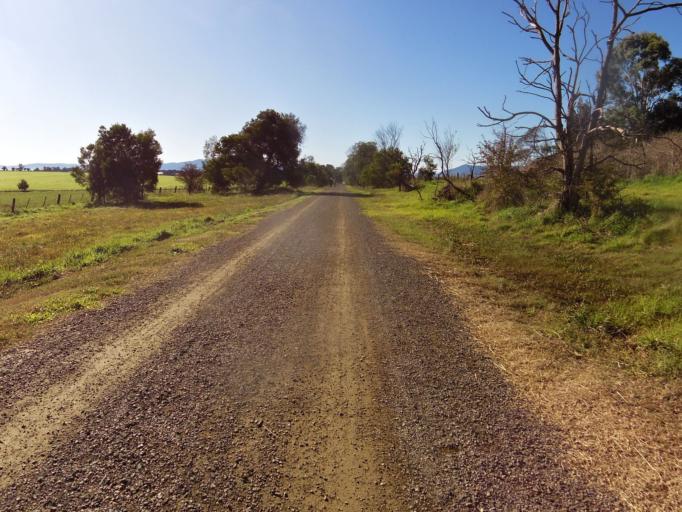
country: AU
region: Victoria
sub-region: Yarra Ranges
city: Lilydale
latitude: -37.7343
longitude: 145.3666
